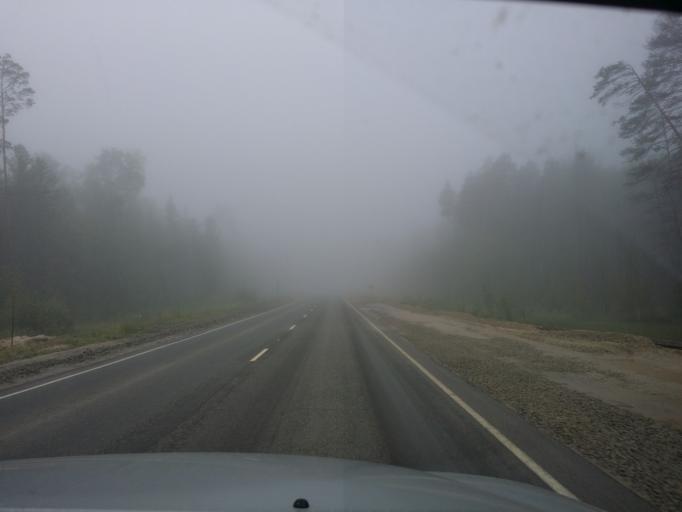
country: RU
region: Khanty-Mansiyskiy Avtonomnyy Okrug
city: Gornopravdinsk
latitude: 59.6508
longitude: 69.9196
